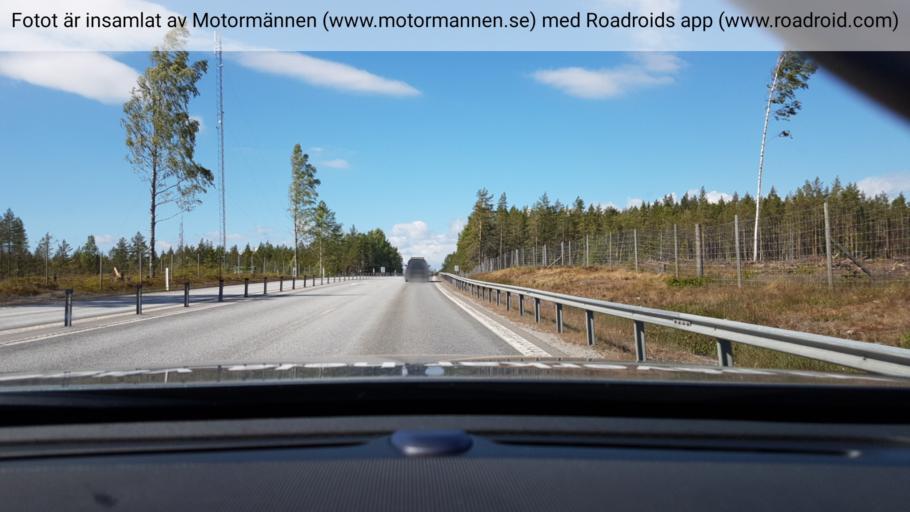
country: SE
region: Vaesterbotten
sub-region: Nordmalings Kommun
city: Nordmaling
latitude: 63.5846
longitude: 19.6332
